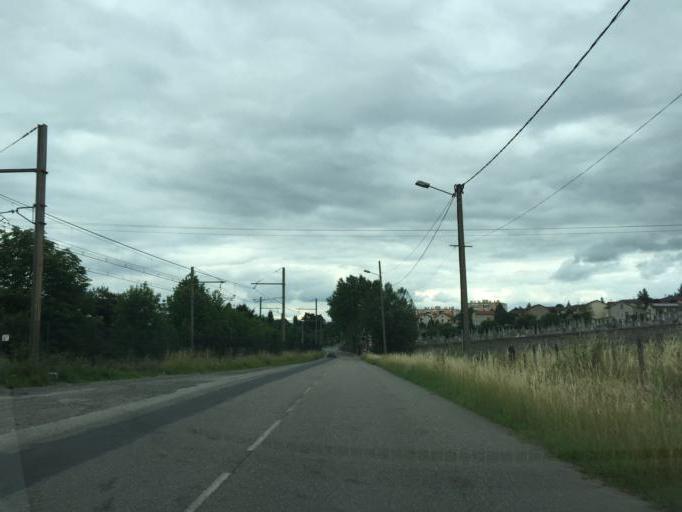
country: FR
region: Rhone-Alpes
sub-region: Departement de la Loire
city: Saint-Chamond
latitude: 45.4607
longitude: 4.4957
